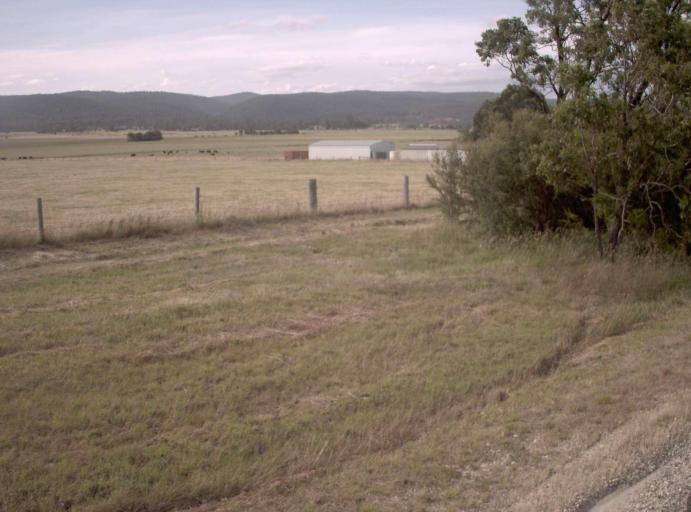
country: AU
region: Victoria
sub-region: Wellington
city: Heyfield
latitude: -38.0241
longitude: 146.6692
